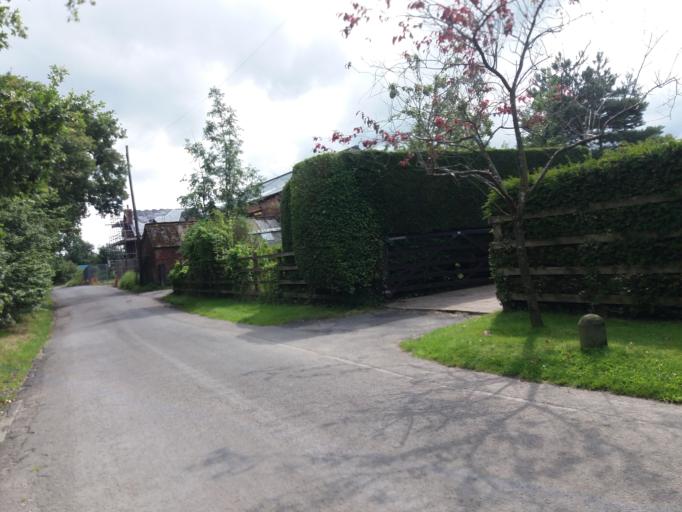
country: GB
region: England
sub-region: Lancashire
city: Euxton
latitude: 53.6668
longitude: -2.6671
